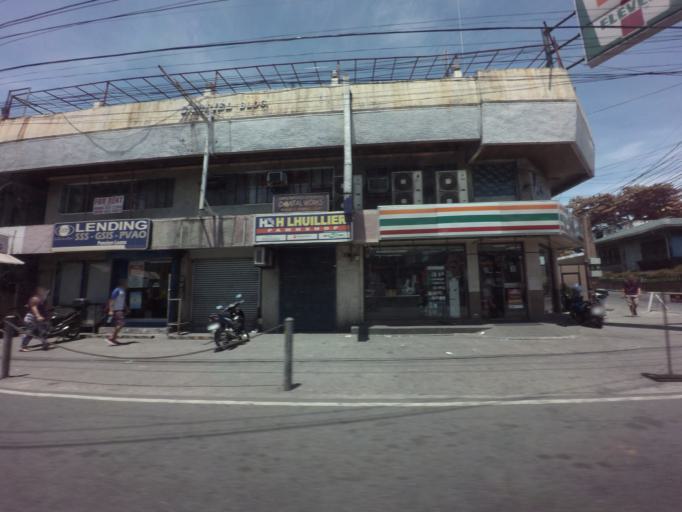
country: PH
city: Sambayanihan People's Village
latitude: 14.5046
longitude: 120.9937
